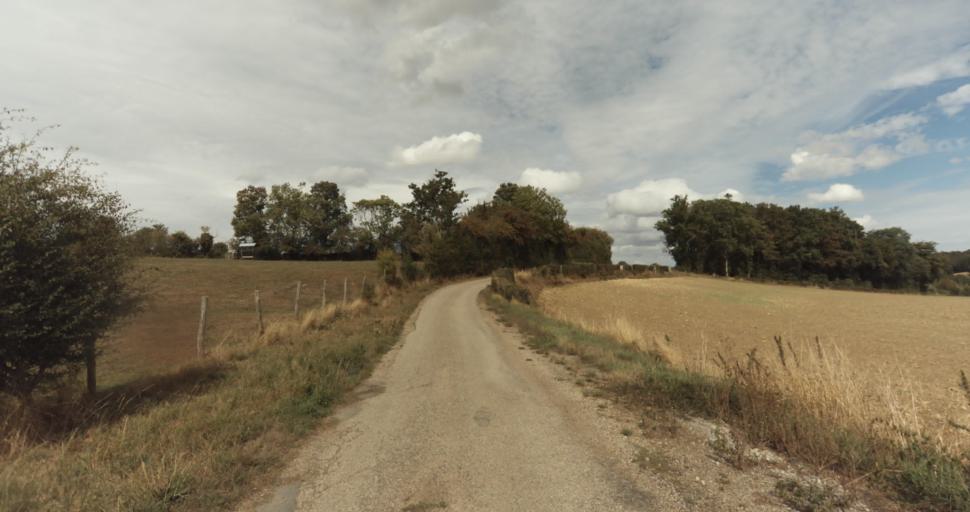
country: FR
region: Lower Normandy
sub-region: Departement du Calvados
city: Orbec
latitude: 48.9111
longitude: 0.3771
